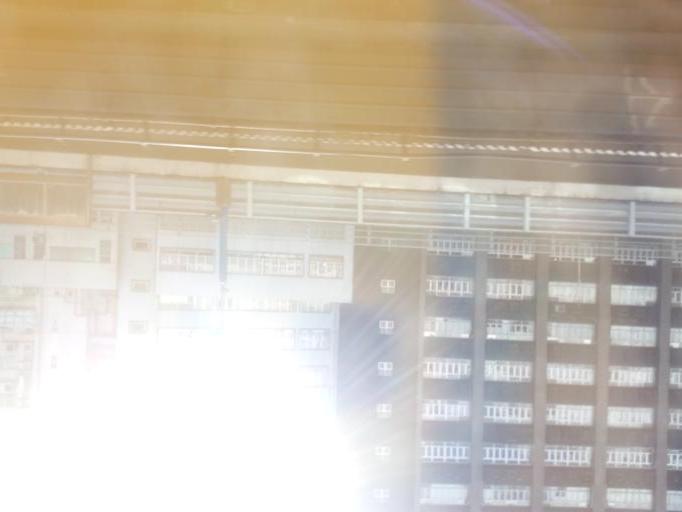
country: HK
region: Kowloon City
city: Kowloon
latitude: 22.3163
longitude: 114.2163
